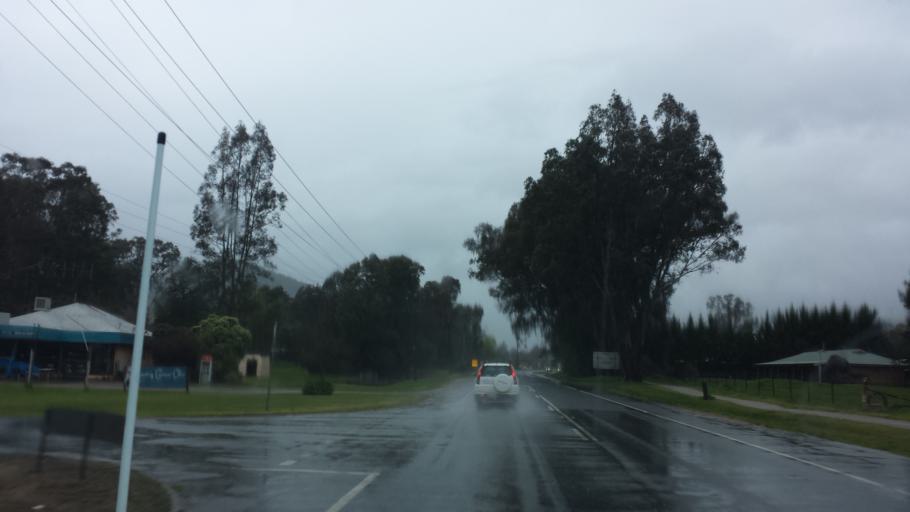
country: AU
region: Victoria
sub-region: Alpine
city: Mount Beauty
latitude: -36.5882
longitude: 146.7609
